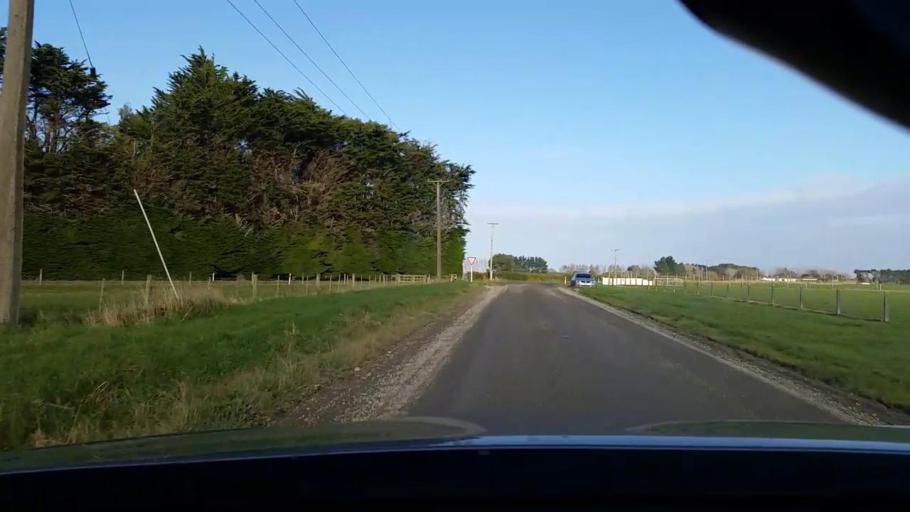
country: NZ
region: Southland
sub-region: Invercargill City
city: Invercargill
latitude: -46.3090
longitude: 168.3036
